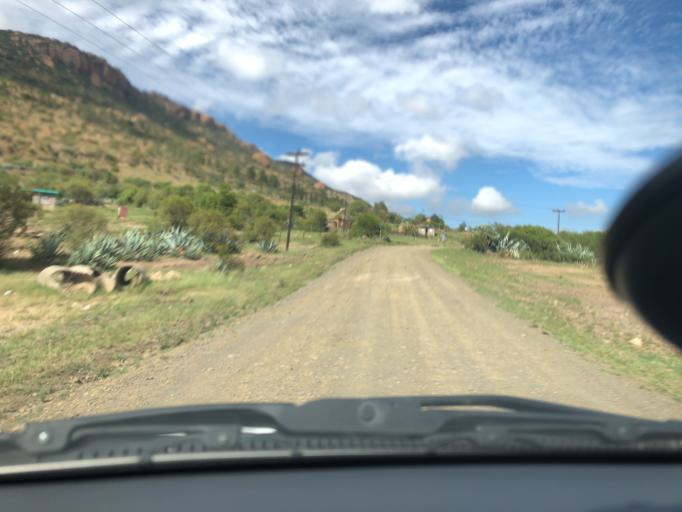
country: LS
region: Maseru
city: Maseru
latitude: -29.4423
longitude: 27.4144
